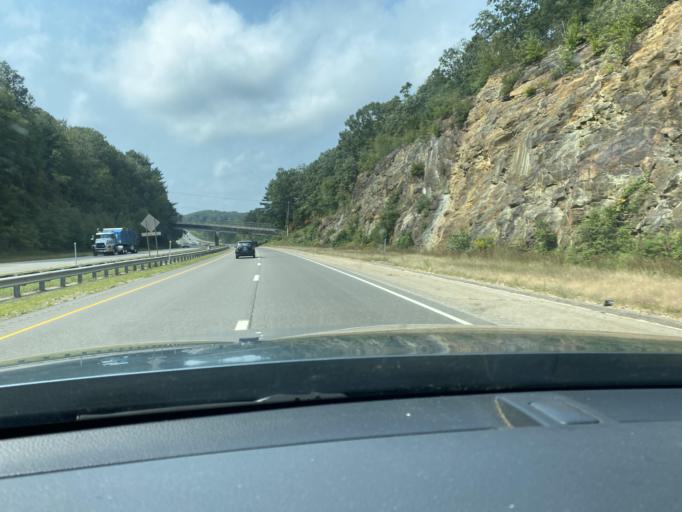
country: US
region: Connecticut
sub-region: New London County
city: Lisbon
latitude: 41.5909
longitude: -72.0163
